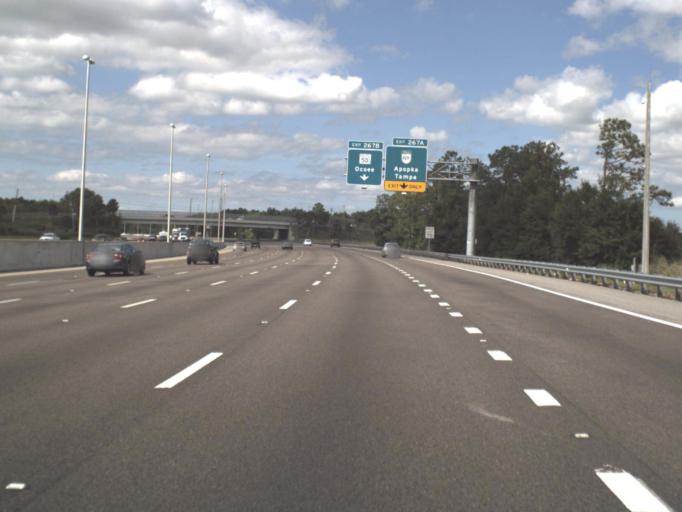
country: US
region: Florida
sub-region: Orange County
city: Gotha
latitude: 28.5444
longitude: -81.5385
